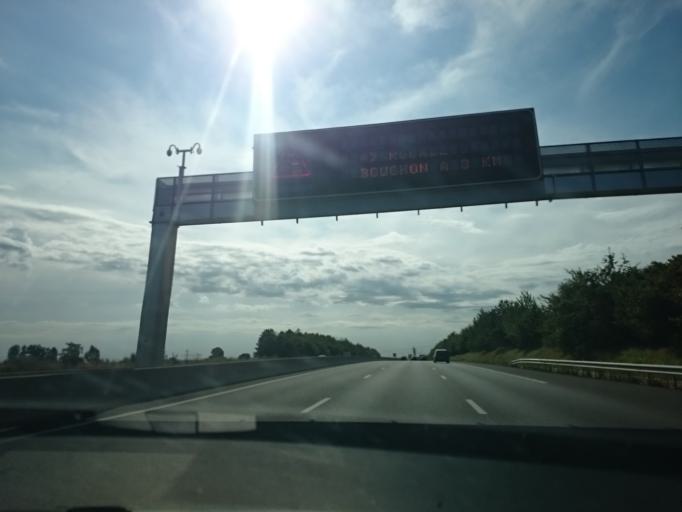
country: FR
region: Brittany
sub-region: Departement d'Ille-et-Vilaine
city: Vezin-le-Coquet
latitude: 48.1335
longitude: -1.7616
